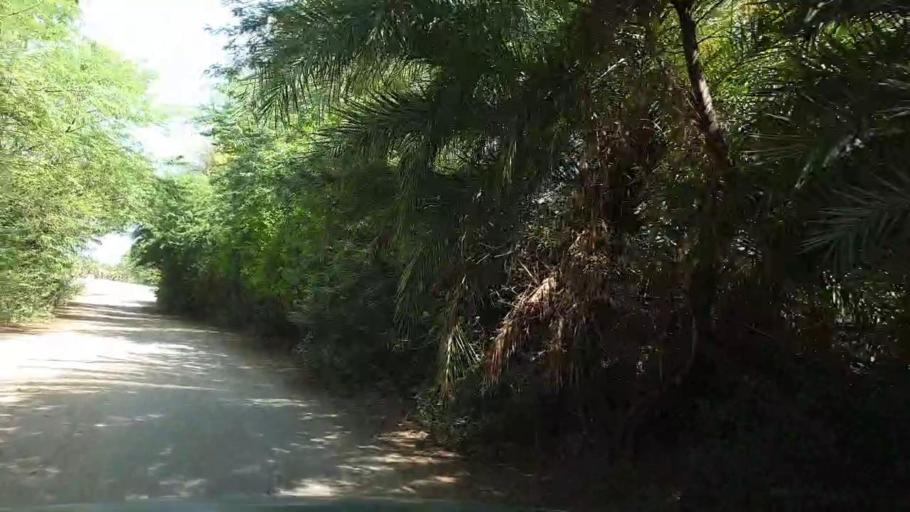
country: PK
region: Sindh
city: Rohri
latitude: 27.6913
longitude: 68.9491
